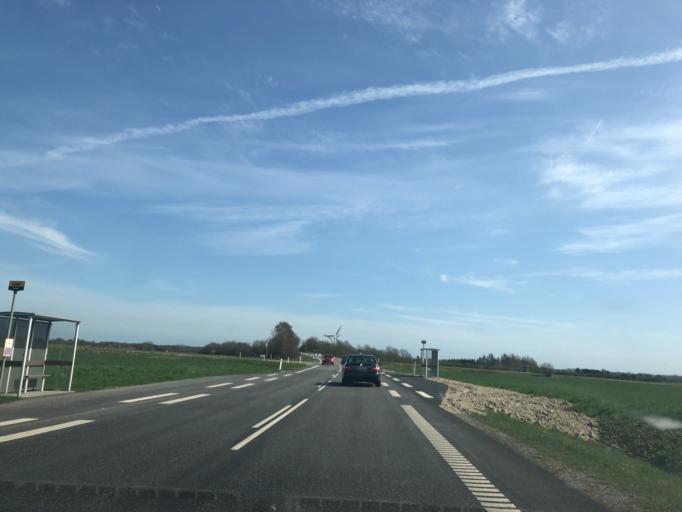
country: DK
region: Zealand
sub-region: Faxe Kommune
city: Ronnede
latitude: 55.2907
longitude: 12.0120
